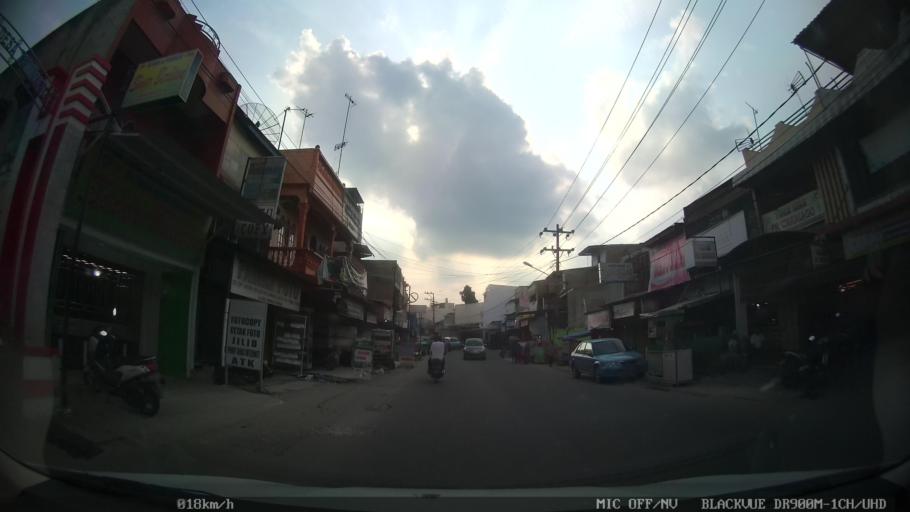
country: ID
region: North Sumatra
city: Medan
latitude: 3.5968
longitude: 98.7473
